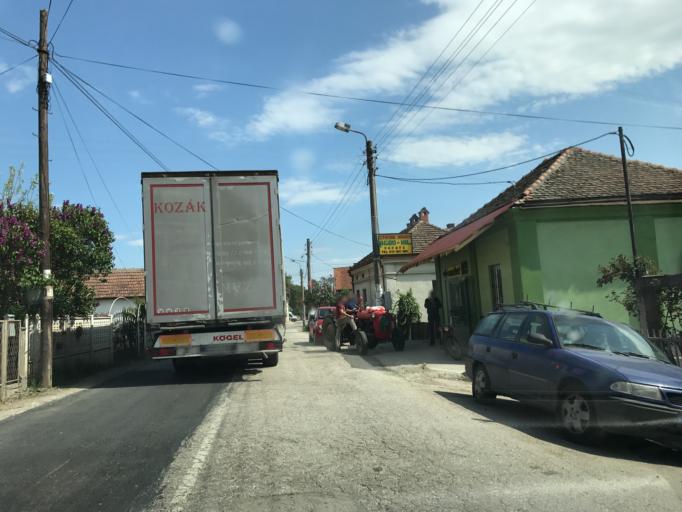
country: RS
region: Central Serbia
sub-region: Zajecarski Okrug
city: Zajecar
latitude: 43.9015
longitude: 22.2151
